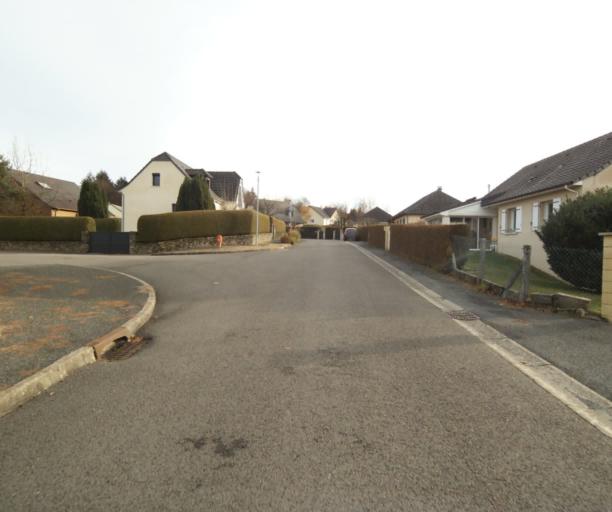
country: FR
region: Limousin
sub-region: Departement de la Correze
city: Sainte-Fortunade
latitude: 45.2020
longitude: 1.7716
